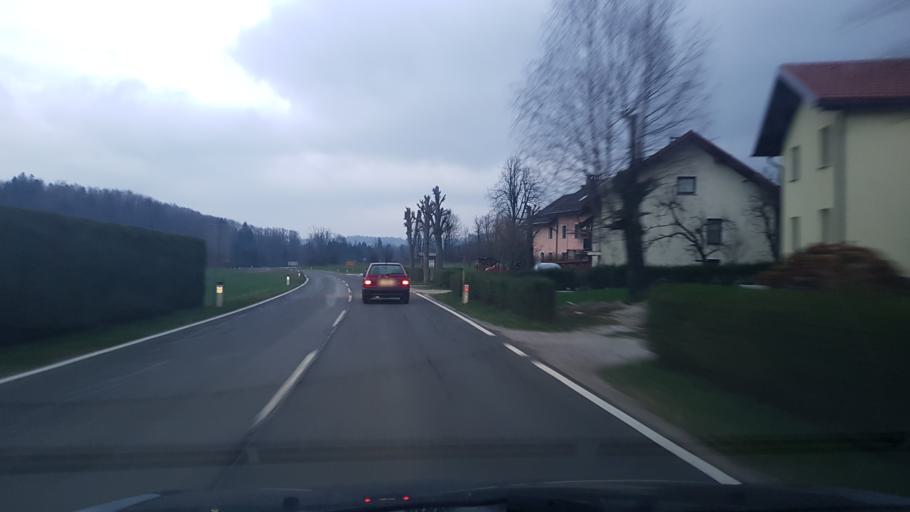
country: SI
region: Idrija
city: Idrija
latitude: 45.9264
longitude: 14.0462
